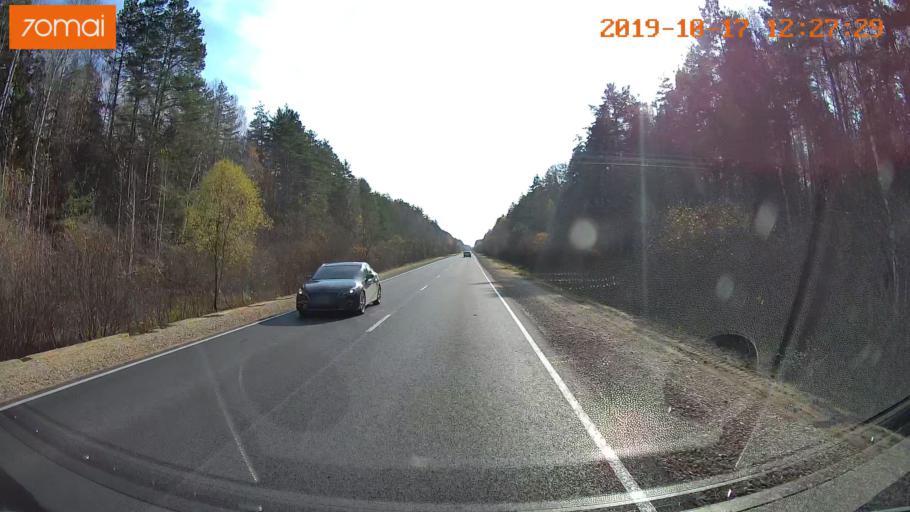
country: RU
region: Rjazan
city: Syntul
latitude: 55.0033
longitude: 41.2632
